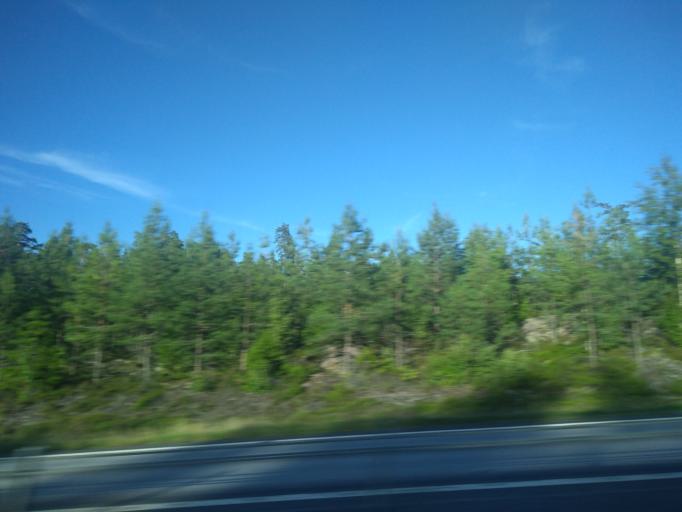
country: SE
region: OEstergoetland
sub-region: Norrkopings Kommun
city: Jursla
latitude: 58.7663
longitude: 16.1691
